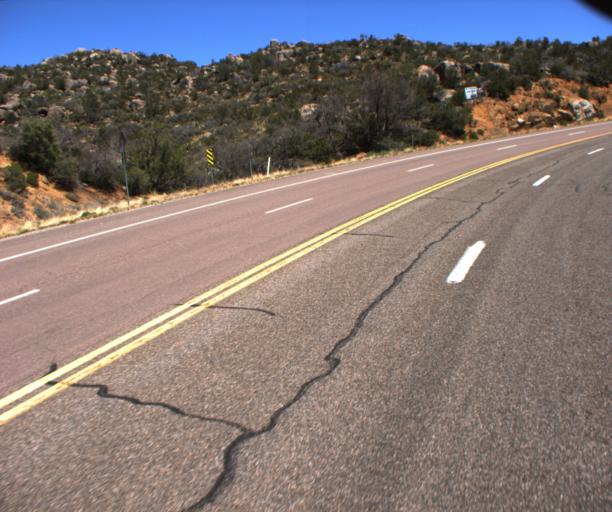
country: US
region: Arizona
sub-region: Yavapai County
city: Congress
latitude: 34.2052
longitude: -112.7577
